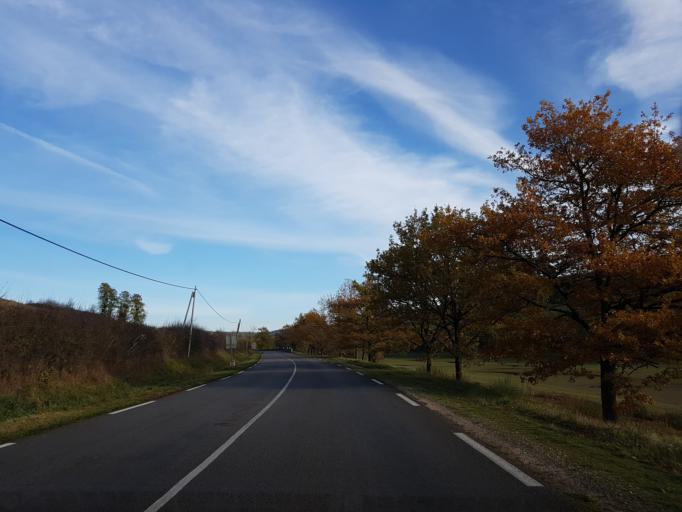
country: FR
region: Bourgogne
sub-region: Departement de la Cote-d'Or
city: Pouilly-en-Auxois
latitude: 47.3092
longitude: 4.6143
